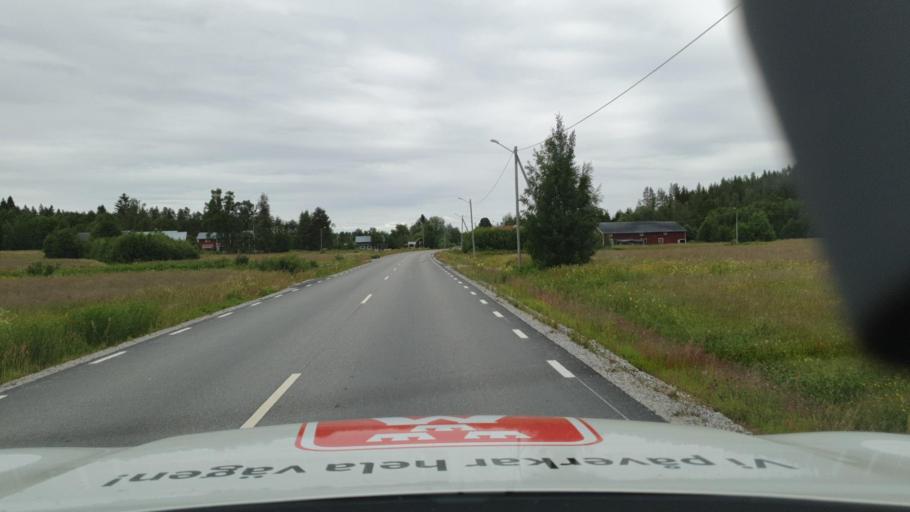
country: SE
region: Vaesterbotten
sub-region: Nordmalings Kommun
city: Nordmaling
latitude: 63.5435
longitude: 19.3711
